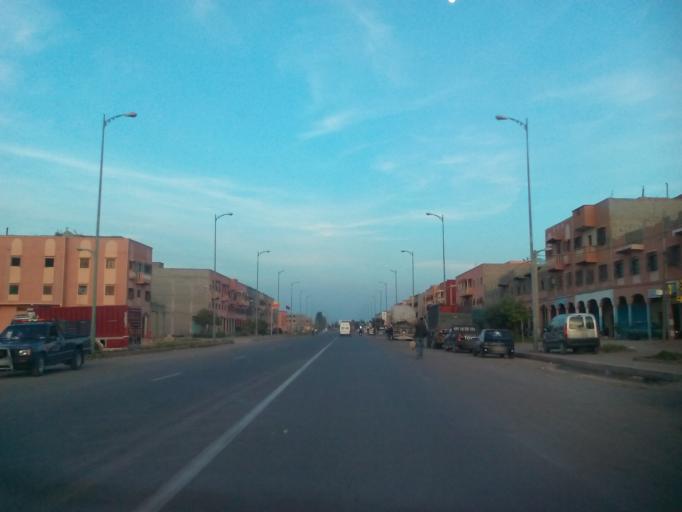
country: MA
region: Marrakech-Tensift-Al Haouz
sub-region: Marrakech
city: Marrakesh
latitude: 31.6344
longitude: -8.2464
